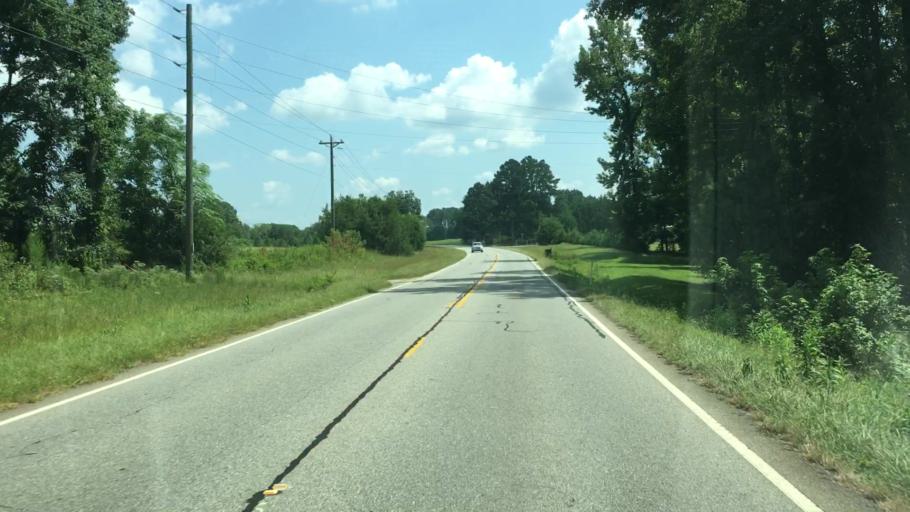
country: US
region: Georgia
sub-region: Oconee County
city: Bogart
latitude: 33.8869
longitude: -83.5574
